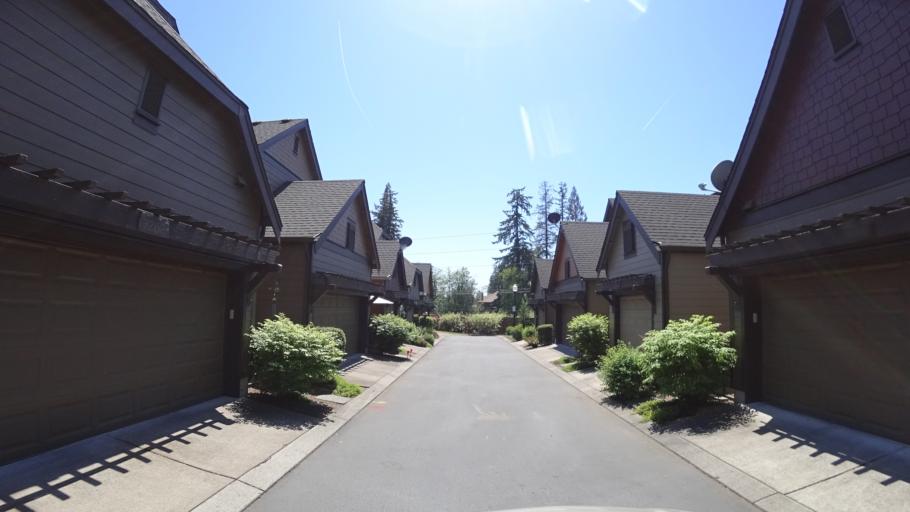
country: US
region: Oregon
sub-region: Washington County
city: Rockcreek
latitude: 45.5287
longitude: -122.9045
